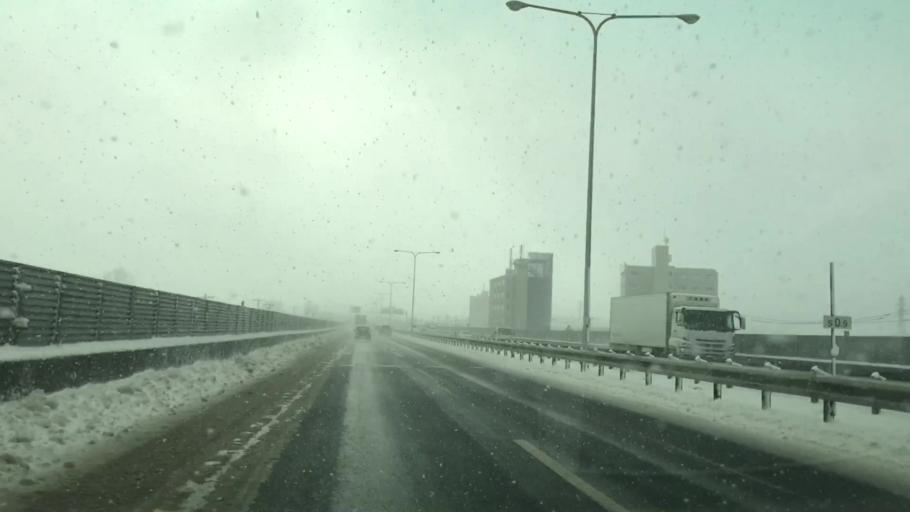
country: JP
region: Hokkaido
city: Sapporo
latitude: 43.0689
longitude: 141.4226
